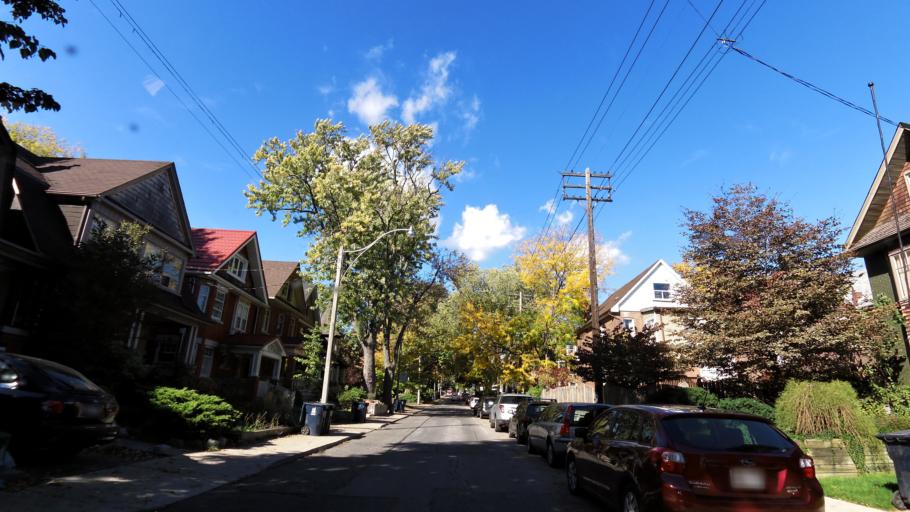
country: CA
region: Ontario
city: Toronto
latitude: 43.6479
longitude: -79.4522
